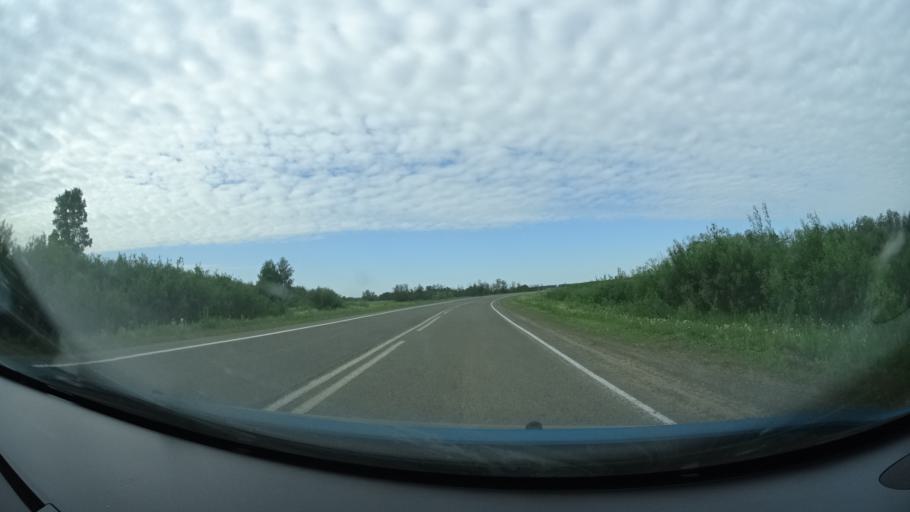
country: RU
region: Perm
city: Kuyeda
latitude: 56.5048
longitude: 55.6259
